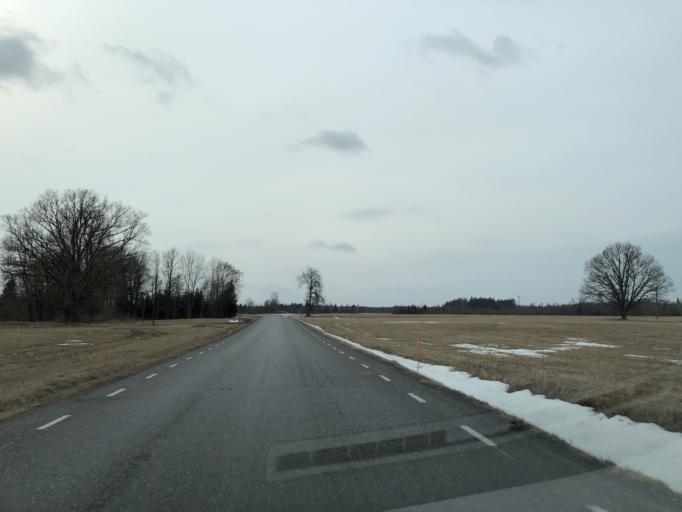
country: EE
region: Paernumaa
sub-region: Vaendra vald (alev)
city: Vandra
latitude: 58.6802
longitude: 25.0041
